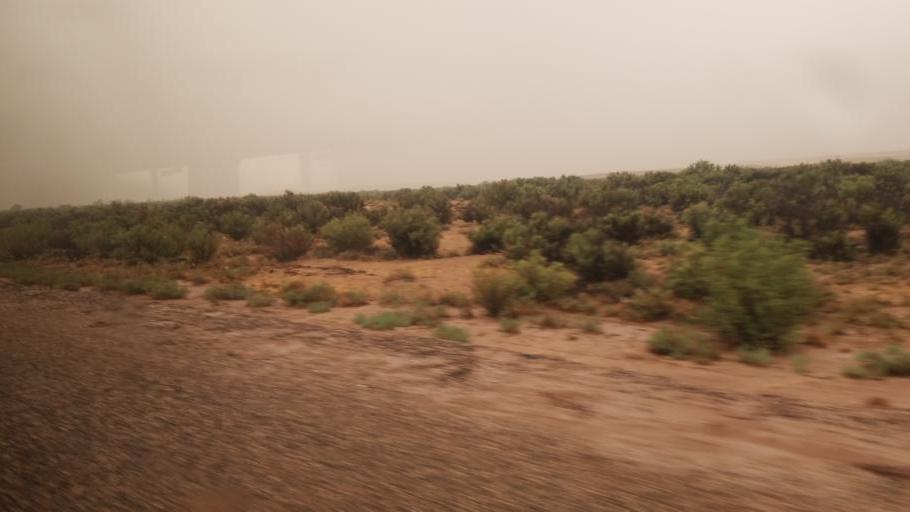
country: US
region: Arizona
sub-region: Navajo County
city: Joseph City
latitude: 34.9545
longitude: -110.3571
